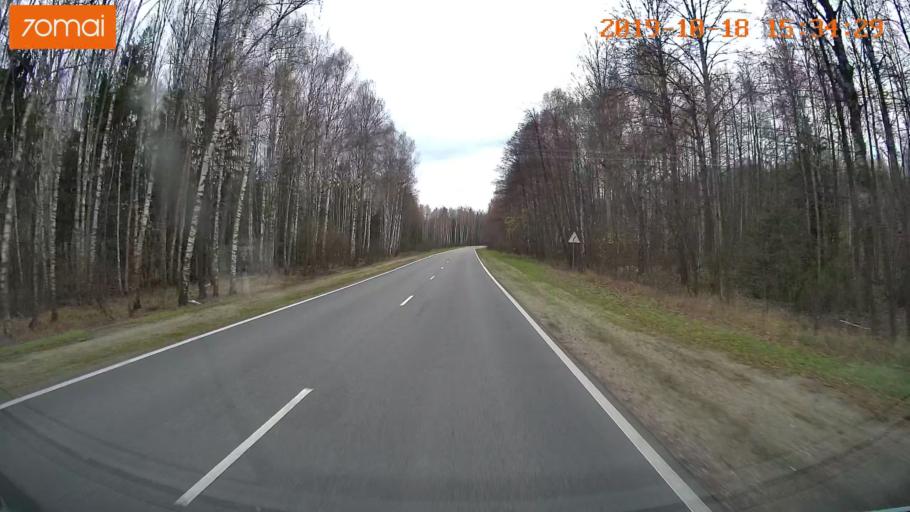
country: RU
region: Vladimir
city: Anopino
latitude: 55.8549
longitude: 40.6418
